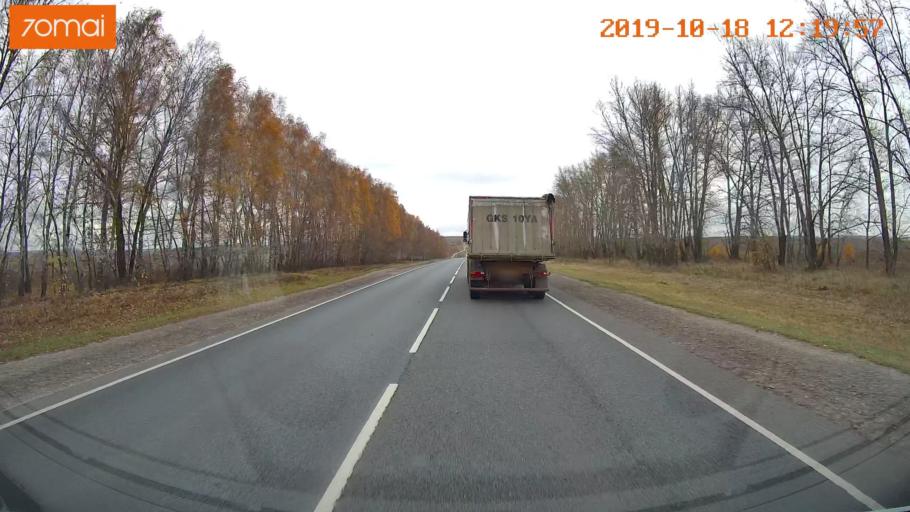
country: RU
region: Rjazan
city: Zakharovo
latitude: 54.4900
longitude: 39.4741
